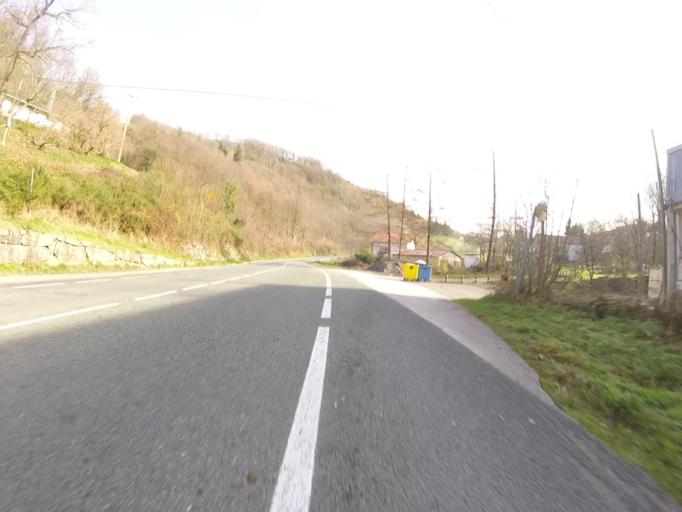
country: ES
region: Navarre
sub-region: Provincia de Navarra
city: Leitza
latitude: 43.0902
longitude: -1.9295
